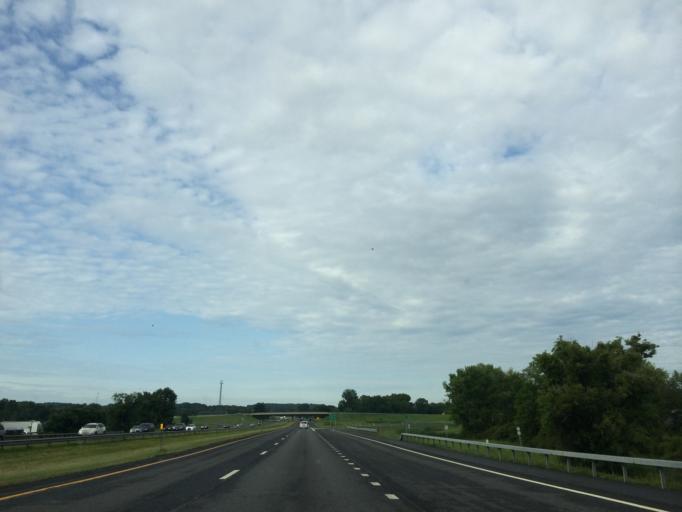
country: US
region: New York
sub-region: Ulster County
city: Lincoln Park
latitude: 41.9517
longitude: -74.0221
